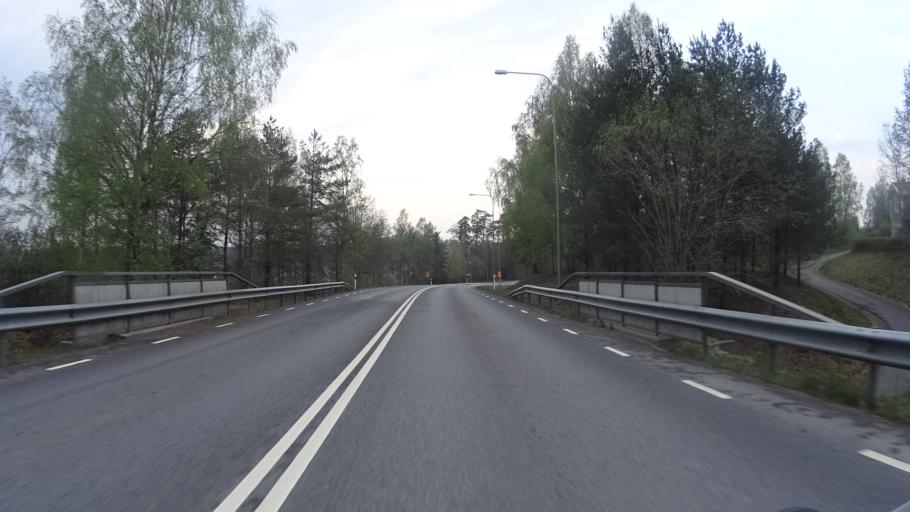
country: SE
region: Kronoberg
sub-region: Ljungby Kommun
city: Ljungby
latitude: 56.8341
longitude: 13.9726
